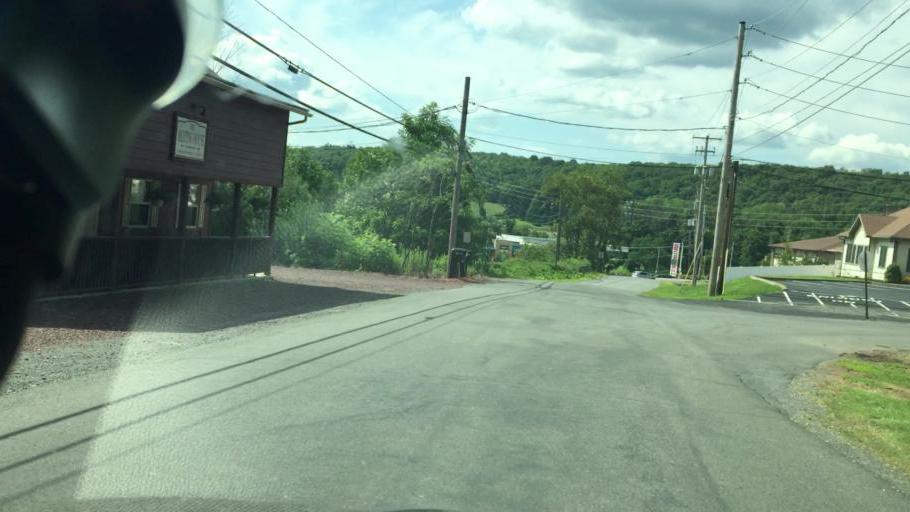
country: US
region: Pennsylvania
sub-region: Luzerne County
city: Harleigh
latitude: 41.0215
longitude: -75.9609
